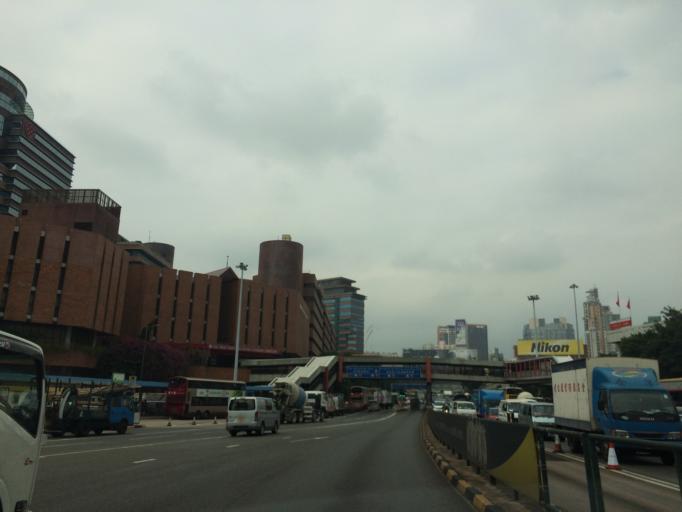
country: HK
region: Kowloon City
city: Kowloon
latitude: 22.3025
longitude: 114.1802
